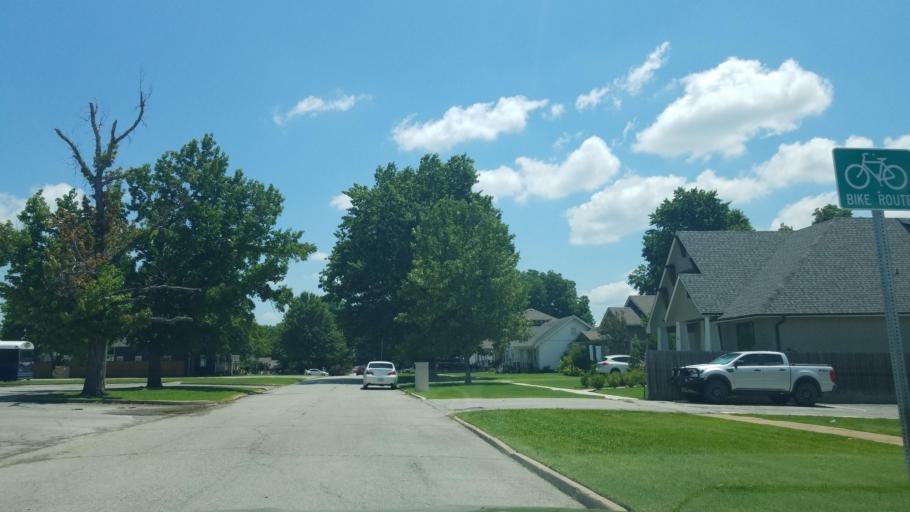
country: US
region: Oklahoma
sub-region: Tulsa County
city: Broken Arrow
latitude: 36.0514
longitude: -95.7894
